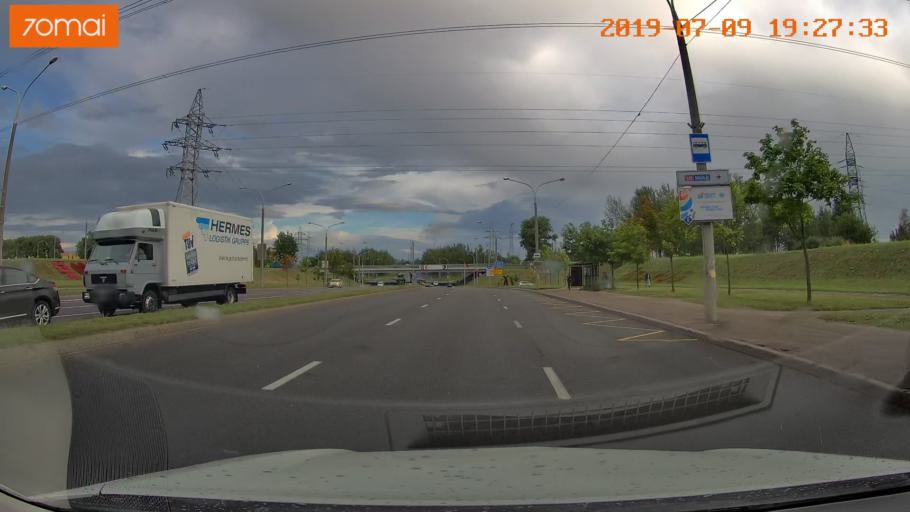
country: BY
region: Minsk
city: Syenitsa
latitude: 53.8352
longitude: 27.5744
